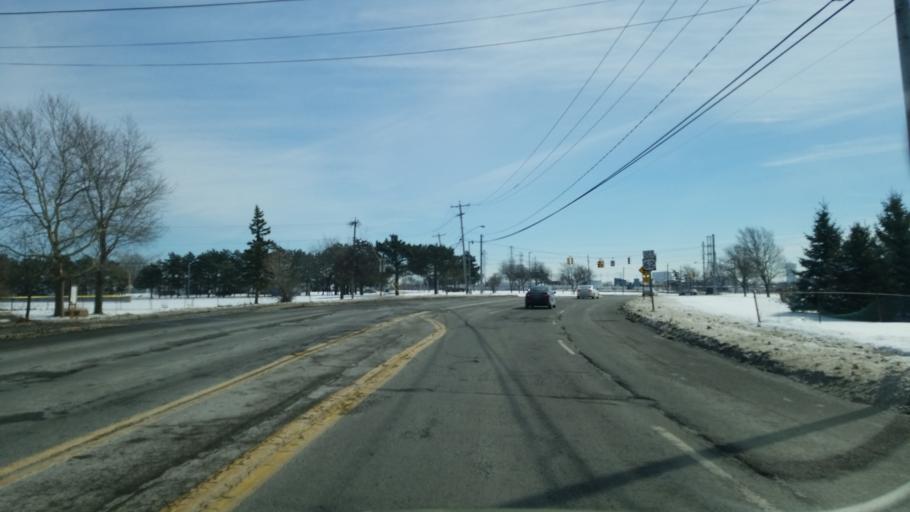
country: US
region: New York
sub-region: Niagara County
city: Niagara Falls
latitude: 43.0951
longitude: -79.0170
